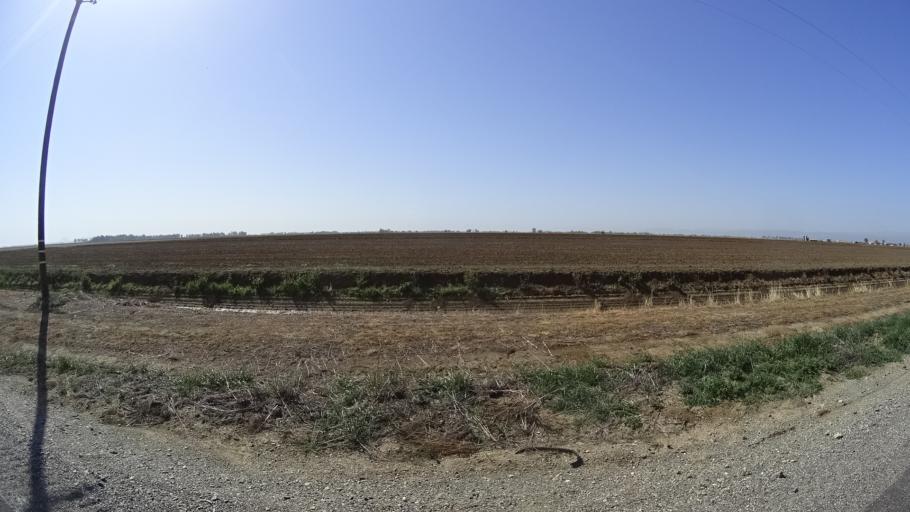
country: US
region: California
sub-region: Glenn County
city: Willows
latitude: 39.4656
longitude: -122.1392
